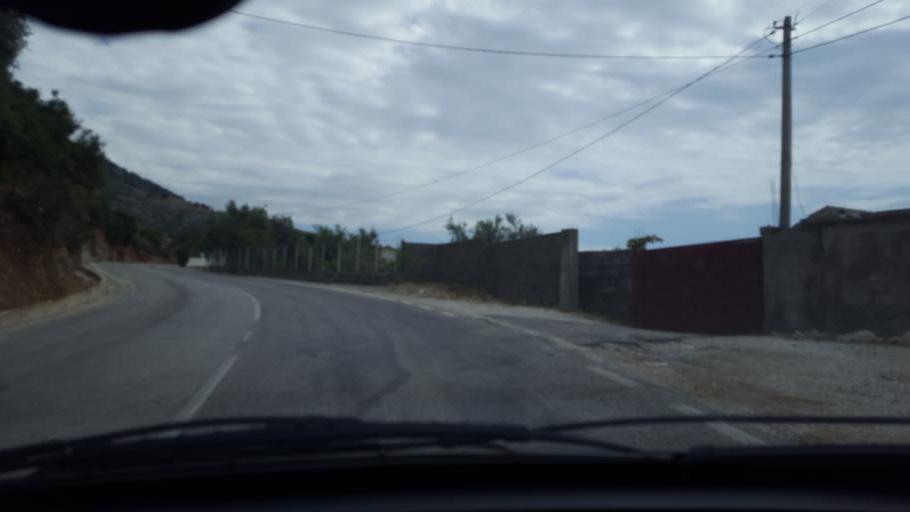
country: AL
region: Vlore
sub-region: Rrethi i Sarandes
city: Lukove
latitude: 40.0585
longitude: 19.8597
